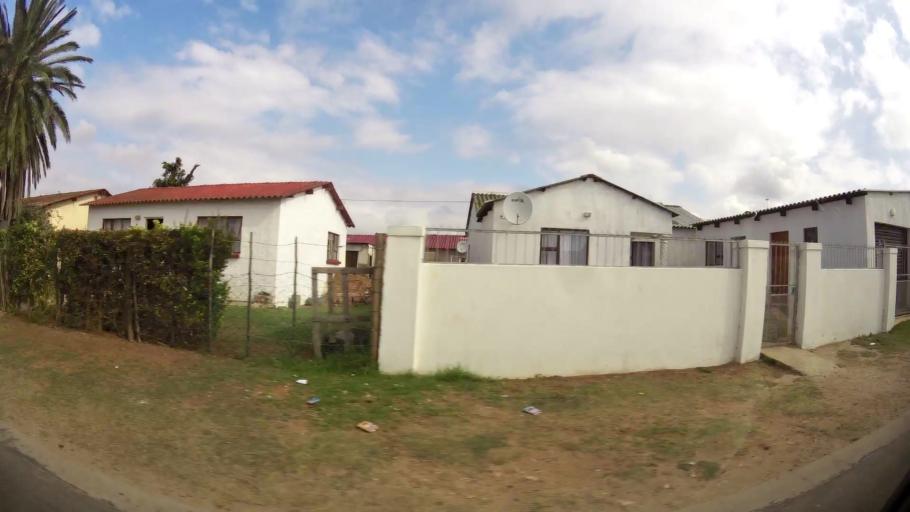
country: ZA
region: Eastern Cape
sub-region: Nelson Mandela Bay Metropolitan Municipality
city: Port Elizabeth
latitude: -33.8092
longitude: 25.5877
